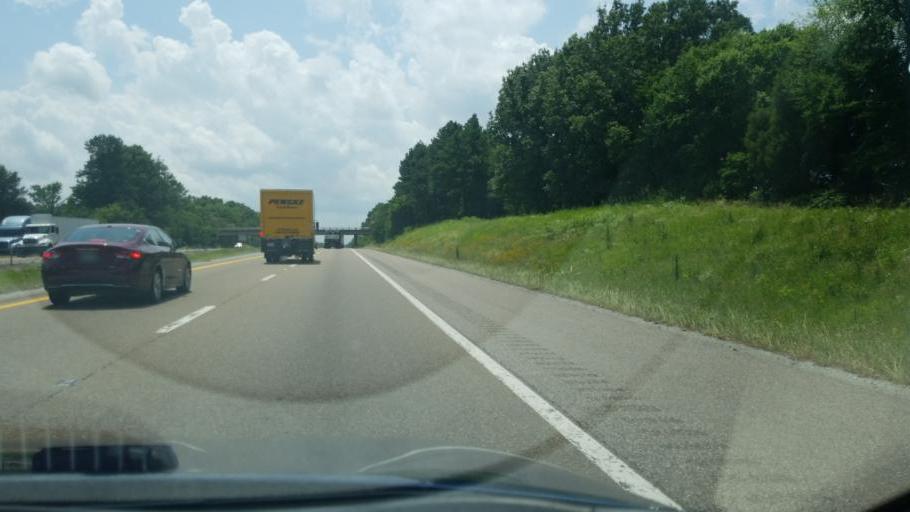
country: US
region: Tennessee
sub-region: Crockett County
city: Bells
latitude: 35.6236
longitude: -88.9803
